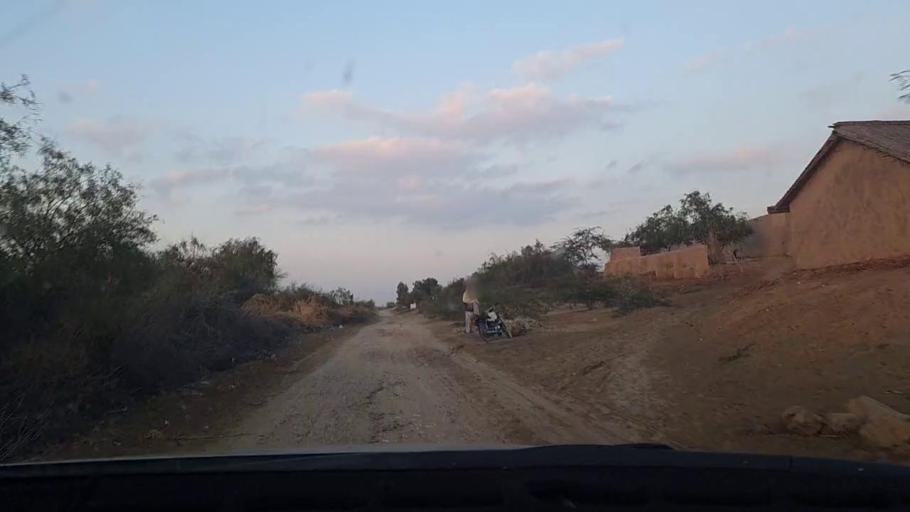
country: PK
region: Sindh
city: Tando Mittha Khan
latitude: 25.9480
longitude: 69.3393
